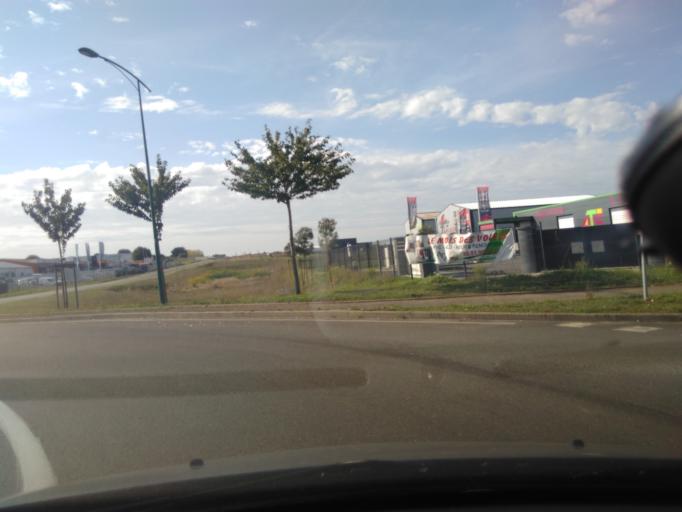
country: FR
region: Pays de la Loire
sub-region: Departement de la Vendee
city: Saint-Hilaire-de-Talmont
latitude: 46.4545
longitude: -1.5954
